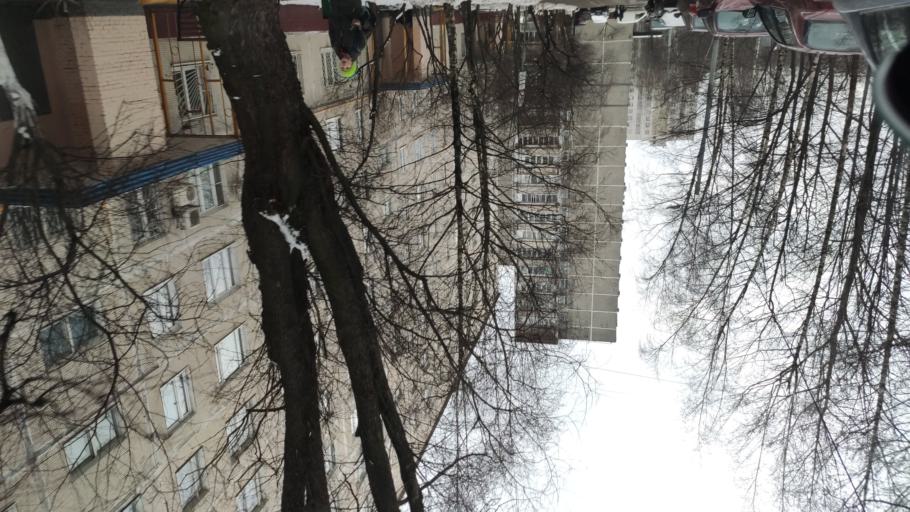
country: RU
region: Moscow
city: Tyoply Stan
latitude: 55.6202
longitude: 37.4908
